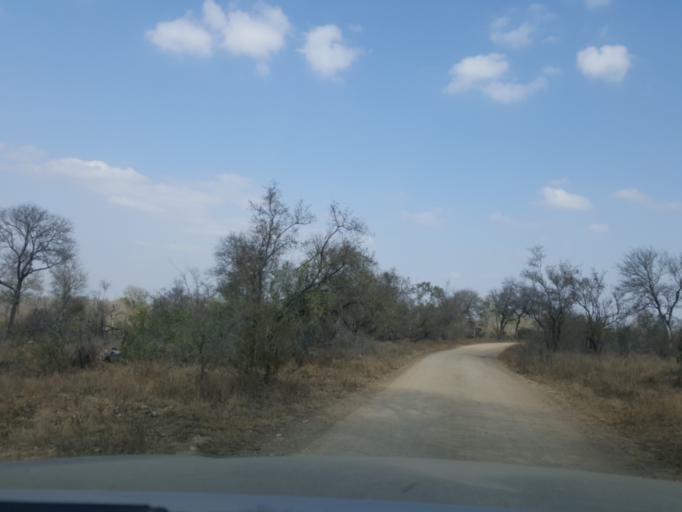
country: ZA
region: Mpumalanga
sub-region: Ehlanzeni District
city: Komatipoort
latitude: -25.2680
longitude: 31.7970
